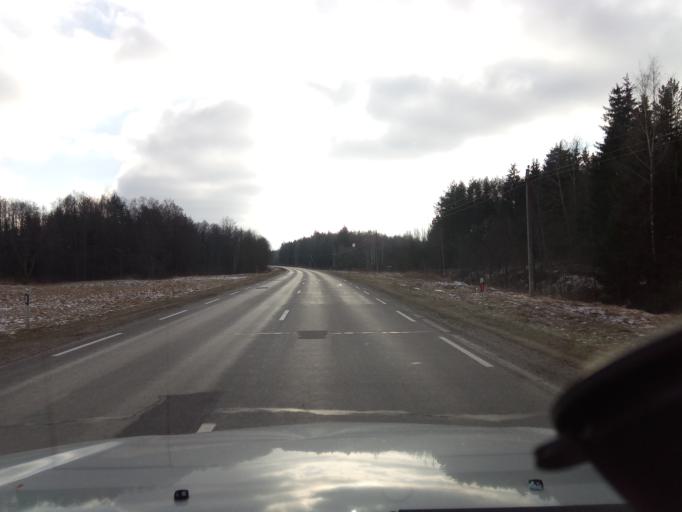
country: LT
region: Alytaus apskritis
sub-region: Alytus
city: Alytus
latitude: 54.3139
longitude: 24.1399
